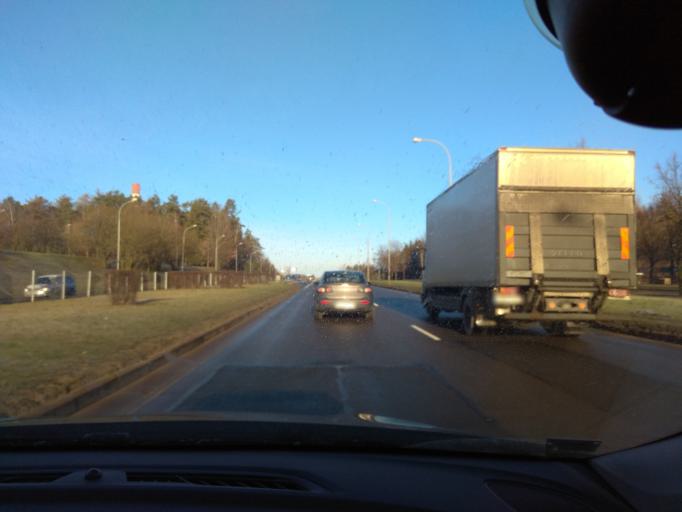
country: LT
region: Vilnius County
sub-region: Vilnius
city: Fabijoniskes
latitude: 54.7310
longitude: 25.2669
